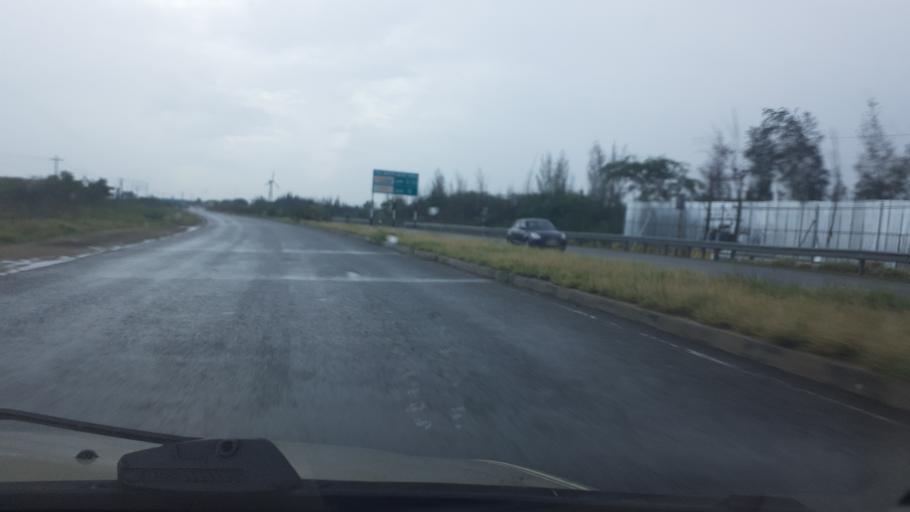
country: IN
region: Tamil Nadu
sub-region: Thoothukkudi
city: Kayattar
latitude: 8.9841
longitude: 77.7759
